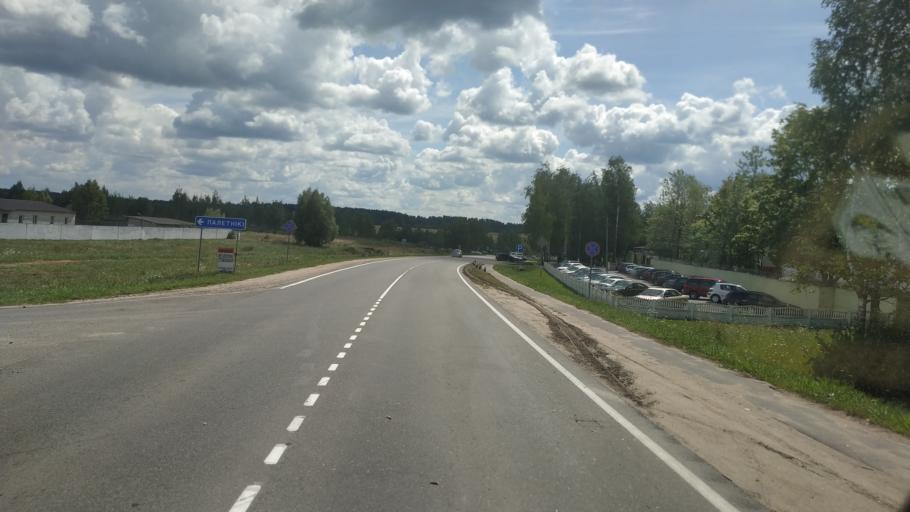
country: BY
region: Mogilev
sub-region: Mahilyowski Rayon
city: Veyno
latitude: 53.8389
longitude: 30.3968
